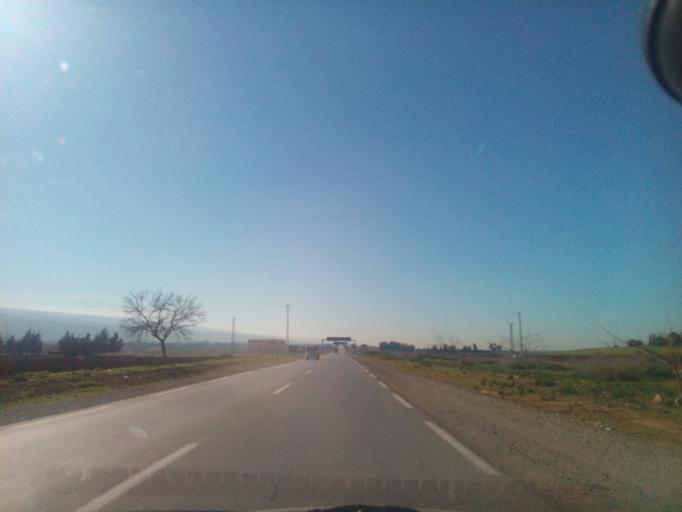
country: DZ
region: Chlef
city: Boukadir
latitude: 36.0327
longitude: 1.0585
